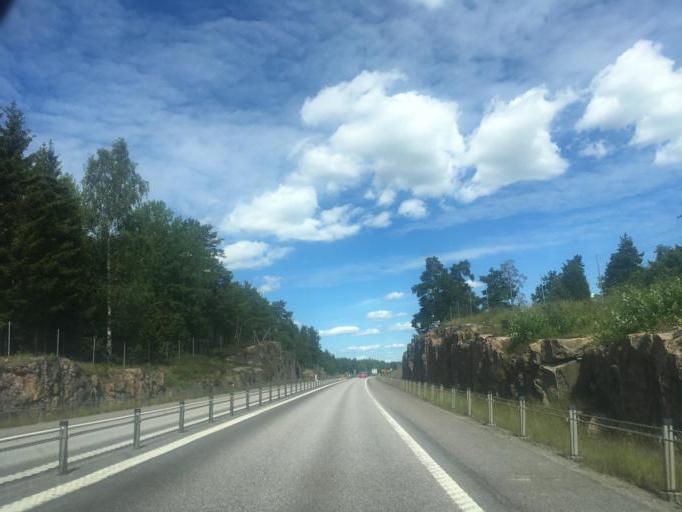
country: SE
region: OEstergoetland
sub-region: Valdemarsviks Kommun
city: Gusum
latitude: 58.3642
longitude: 16.4335
